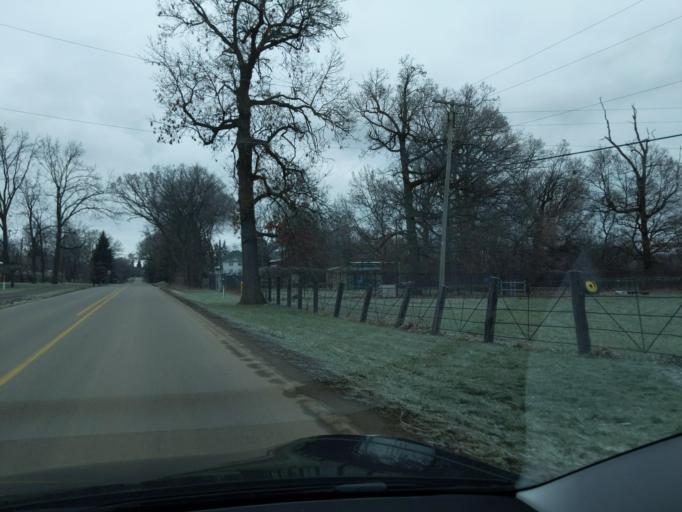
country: US
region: Michigan
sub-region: Jackson County
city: Spring Arbor
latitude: 42.1974
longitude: -84.5536
